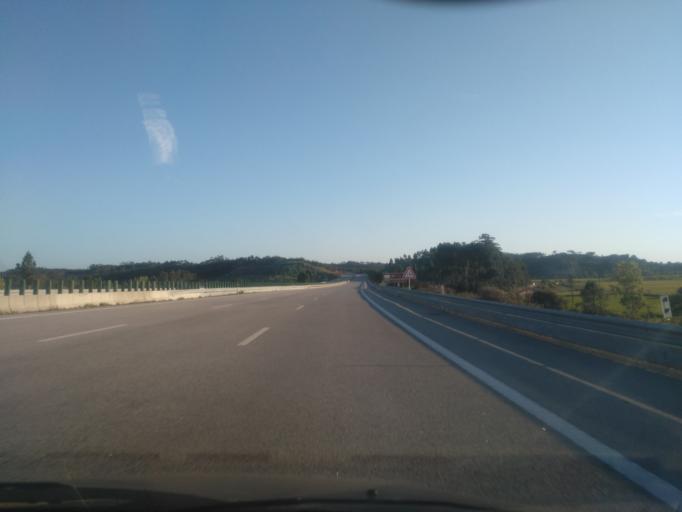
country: PT
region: Coimbra
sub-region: Montemor-O-Velho
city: Montemor-o-Velho
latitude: 40.1300
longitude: -8.7445
